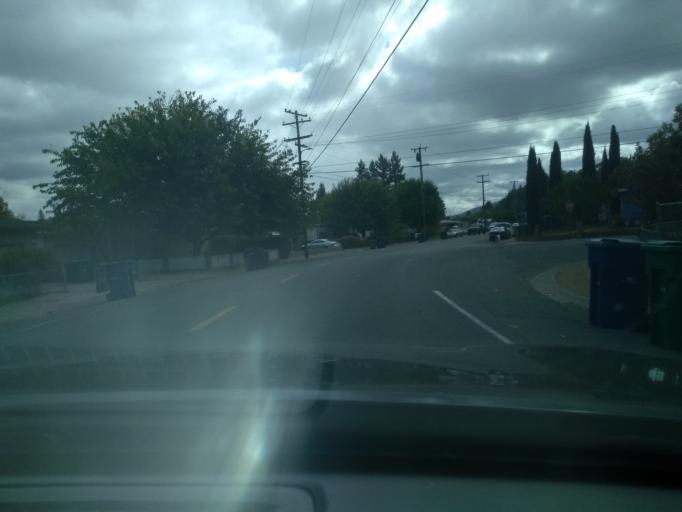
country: US
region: California
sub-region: Mendocino County
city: Ukiah
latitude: 39.1256
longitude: -123.2082
